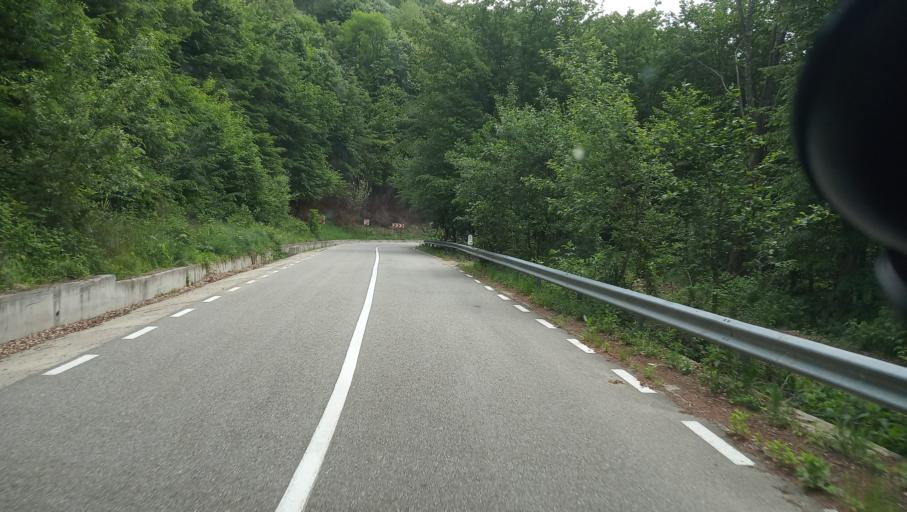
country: RO
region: Caras-Severin
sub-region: Comuna Bucosnita
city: Bucosnita
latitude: 45.2621
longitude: 22.2337
